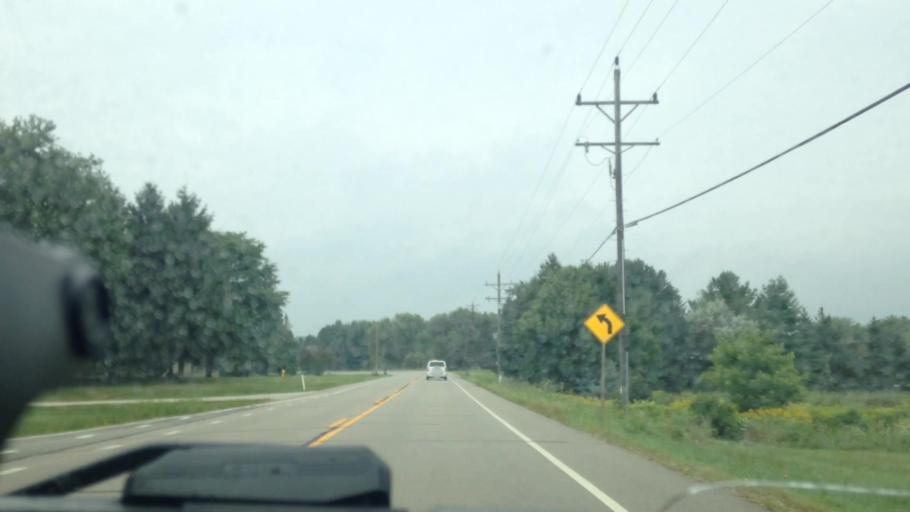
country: US
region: Wisconsin
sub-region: Washington County
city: Slinger
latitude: 43.3439
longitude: -88.3049
